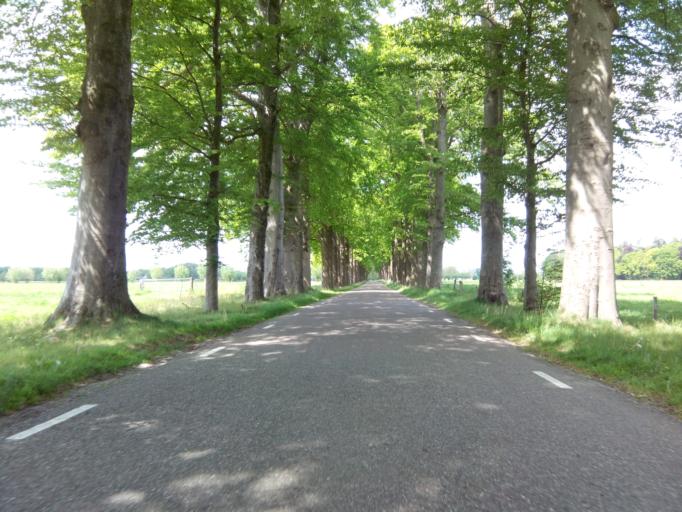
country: NL
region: Utrecht
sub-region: Gemeente Utrechtse Heuvelrug
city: Overberg
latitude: 52.0706
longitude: 5.4726
